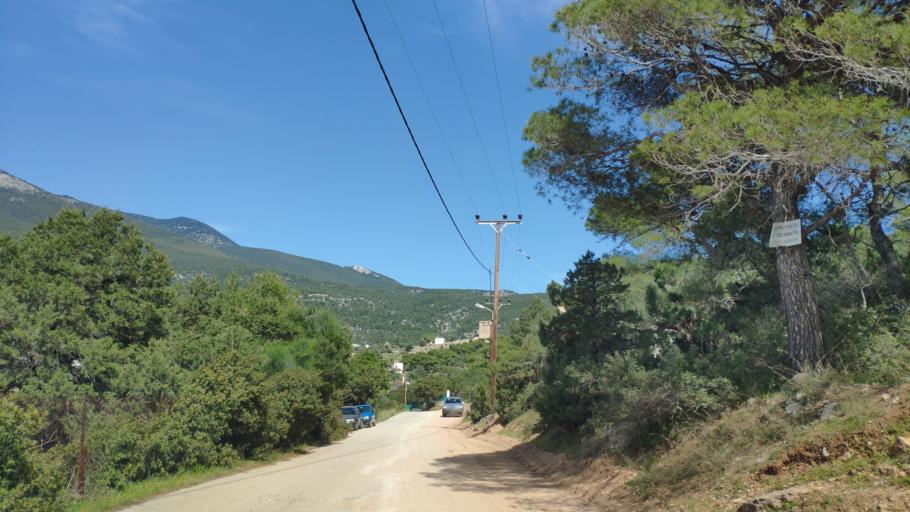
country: GR
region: Central Greece
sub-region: Nomos Voiotias
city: Kaparellion
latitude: 38.1447
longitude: 23.2221
